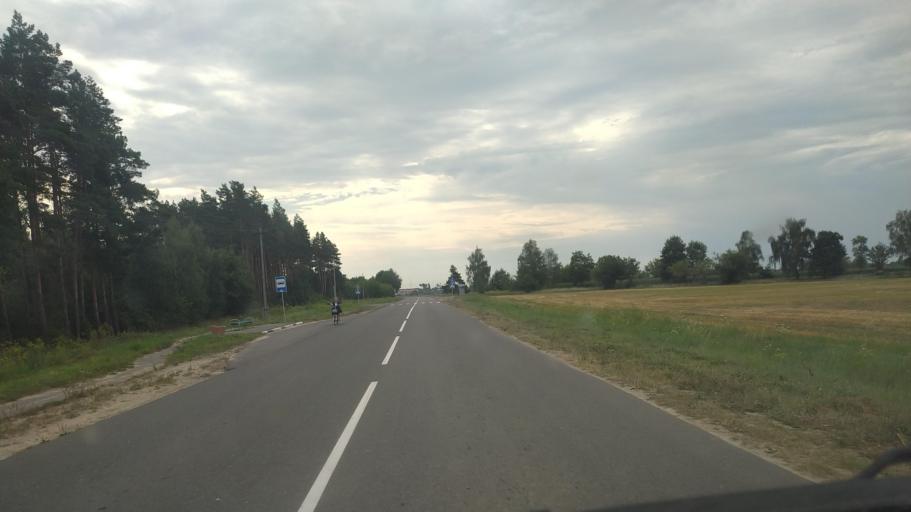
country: BY
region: Brest
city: Byaroza
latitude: 52.5589
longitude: 24.9125
